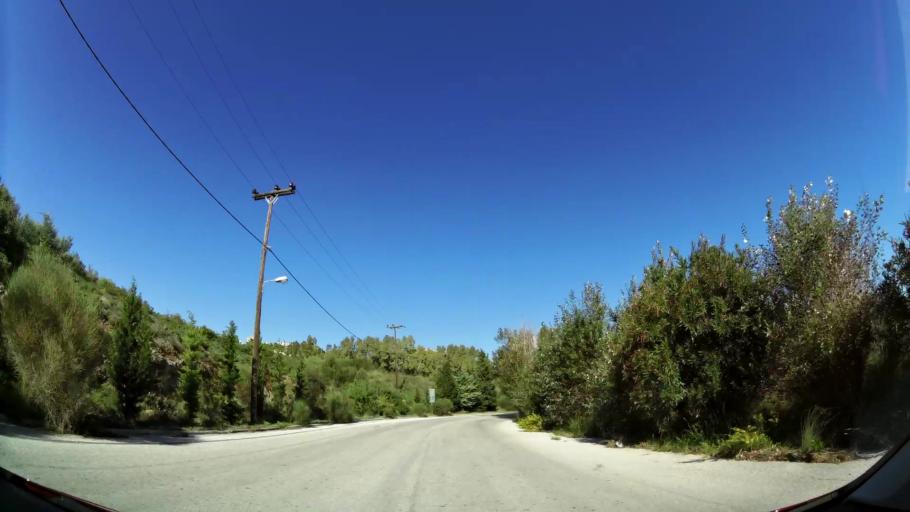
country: GR
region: Attica
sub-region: Nomarchia Anatolikis Attikis
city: Dhrafi
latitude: 38.0312
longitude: 23.9058
